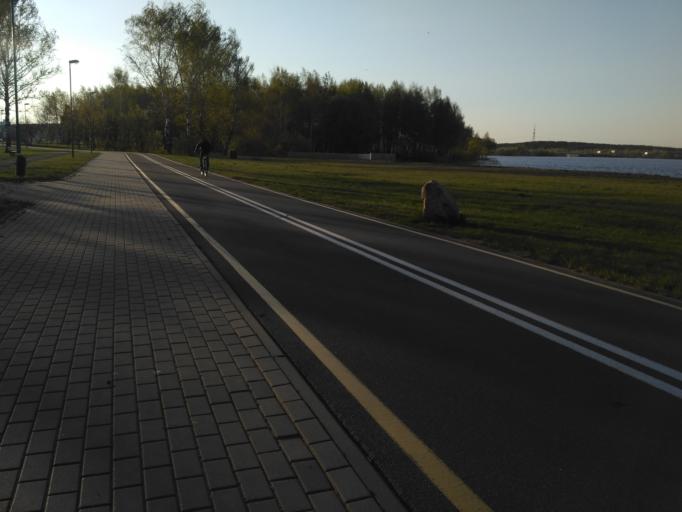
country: BY
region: Minsk
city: Zhdanovichy
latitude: 53.9458
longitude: 27.4596
